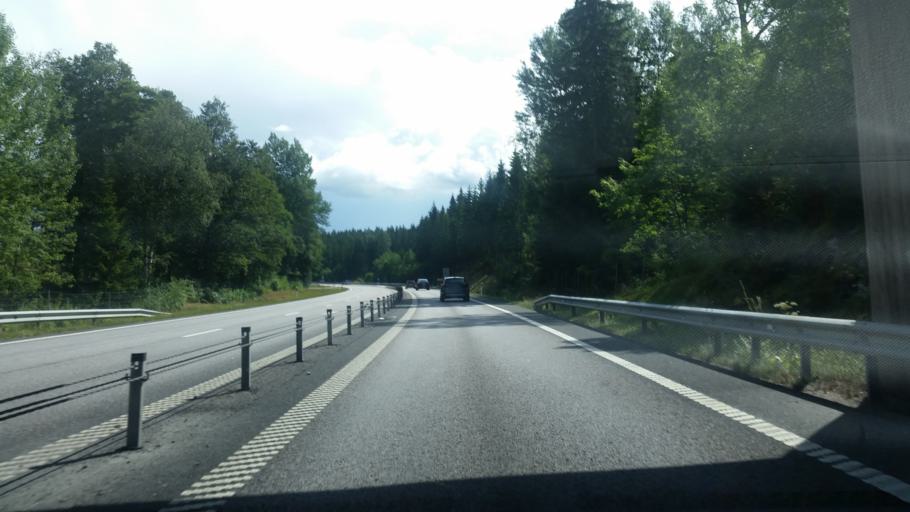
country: SE
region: Joenkoeping
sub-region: Mullsjo Kommun
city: Mullsjoe
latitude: 57.7648
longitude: 13.7285
